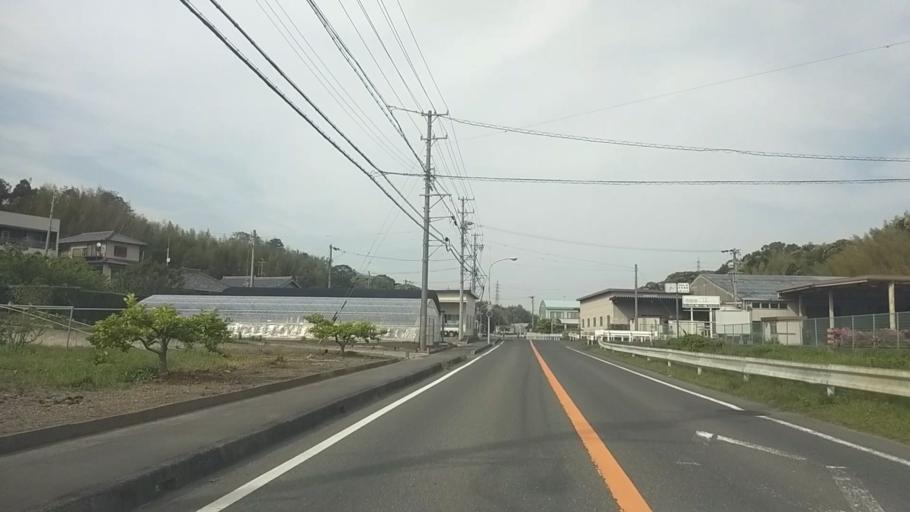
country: JP
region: Shizuoka
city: Hamamatsu
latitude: 34.7157
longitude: 137.6504
